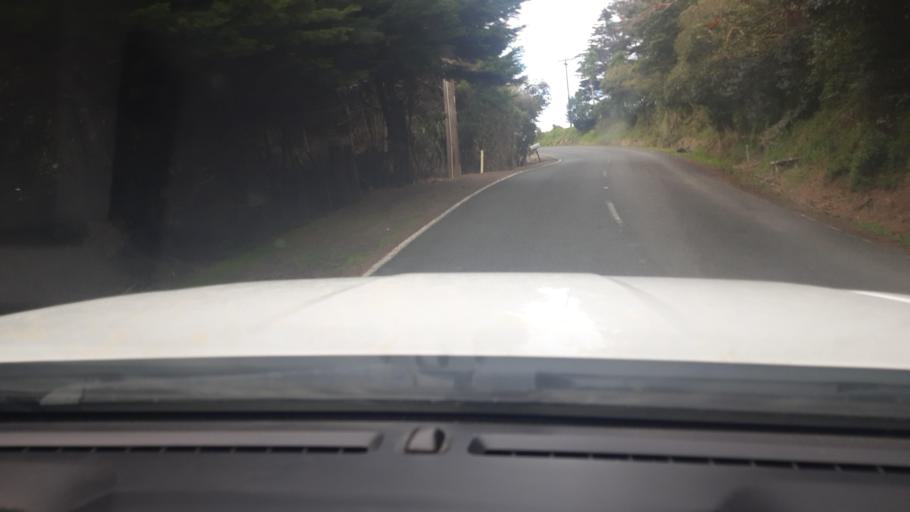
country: NZ
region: Northland
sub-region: Far North District
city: Ahipara
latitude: -35.2714
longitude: 173.2093
